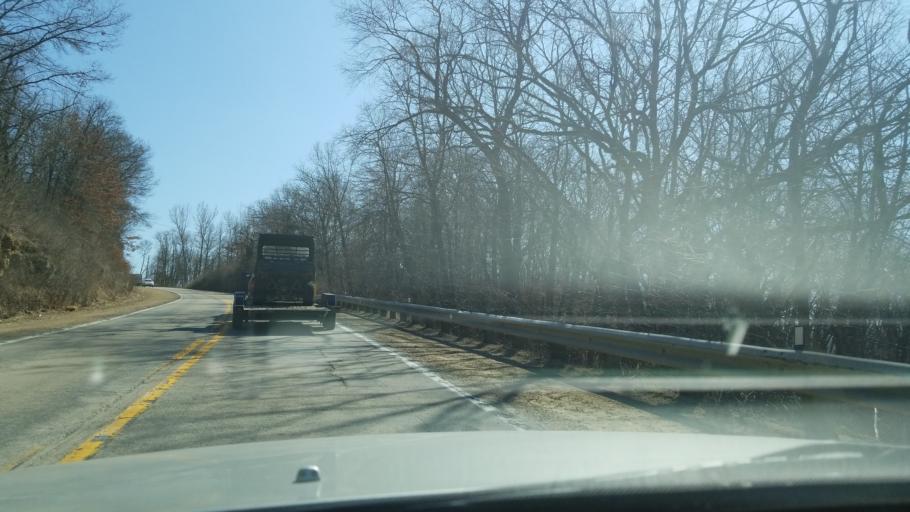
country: US
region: Wisconsin
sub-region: Iowa County
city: Mineral Point
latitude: 42.8642
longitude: -90.2048
